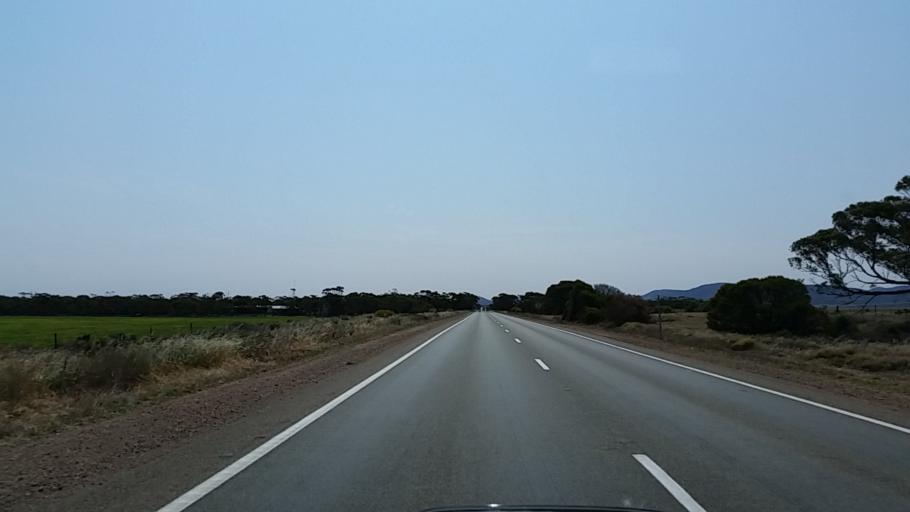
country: AU
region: South Australia
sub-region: Port Pirie City and Dists
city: Port Pirie
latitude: -32.9229
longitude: 137.9824
